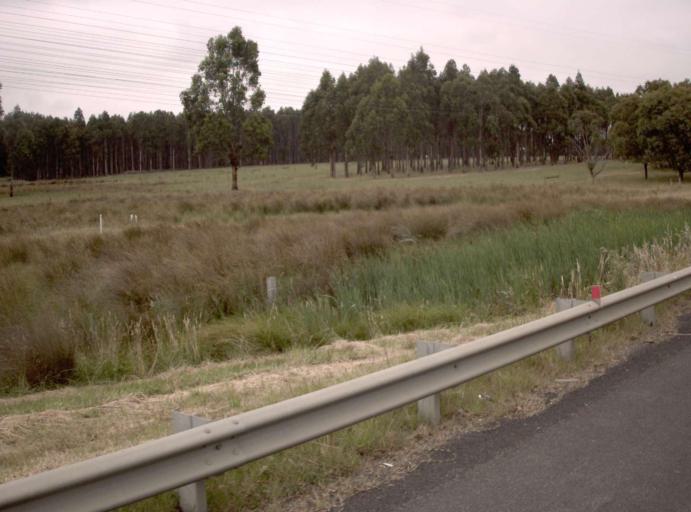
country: AU
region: Victoria
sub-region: Latrobe
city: Morwell
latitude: -38.2779
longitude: 146.4172
